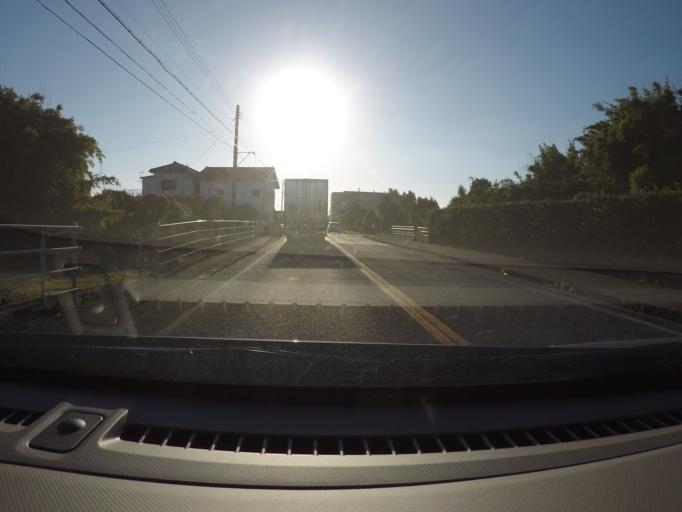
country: JP
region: Kagoshima
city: Izumi
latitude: 32.0987
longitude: 130.3053
